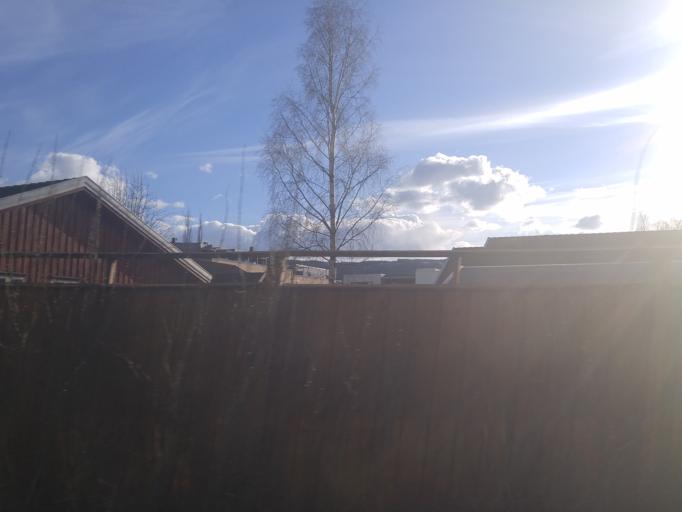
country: NO
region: Oppland
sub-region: Lillehammer
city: Lillehammer
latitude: 61.1201
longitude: 10.4569
